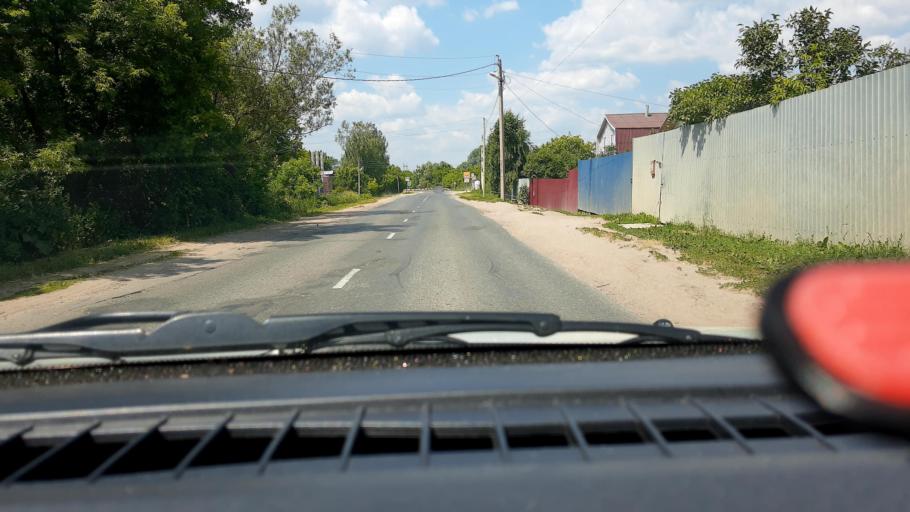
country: RU
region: Nizjnij Novgorod
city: Kstovo
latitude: 56.1310
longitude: 44.0814
